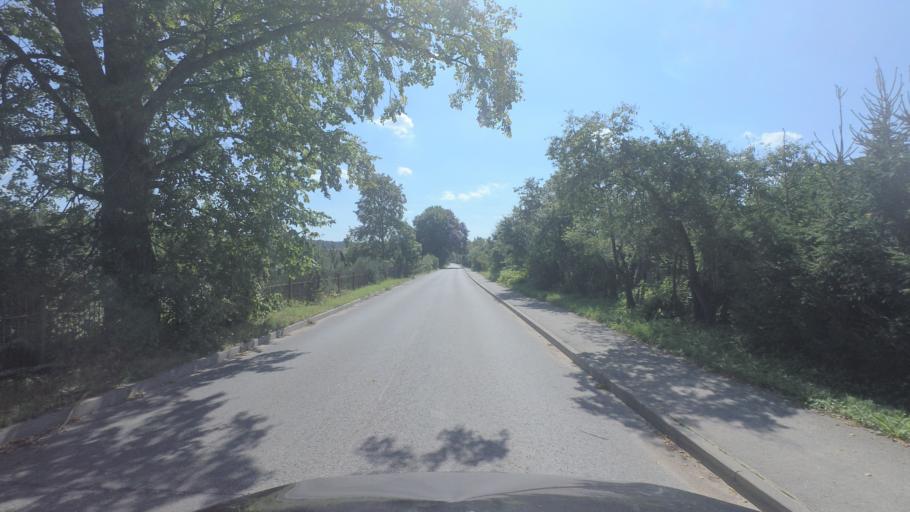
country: LT
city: Nemencine
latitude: 54.8418
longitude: 25.3711
